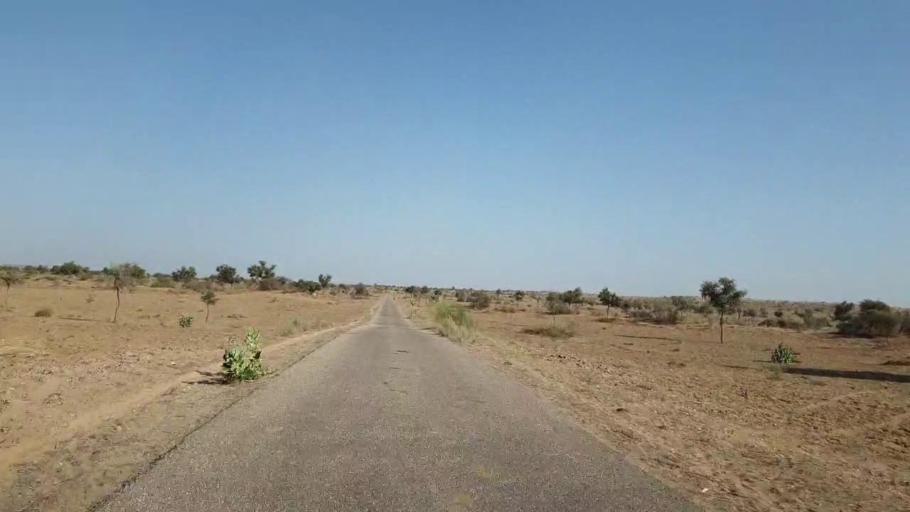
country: PK
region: Sindh
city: Islamkot
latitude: 25.0335
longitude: 70.0339
